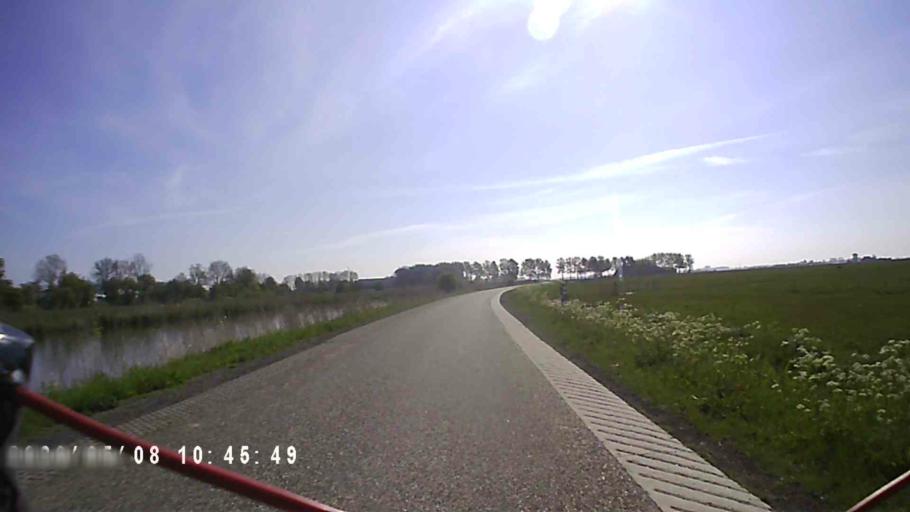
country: NL
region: Groningen
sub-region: Gemeente Winsum
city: Winsum
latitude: 53.3346
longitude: 6.5366
